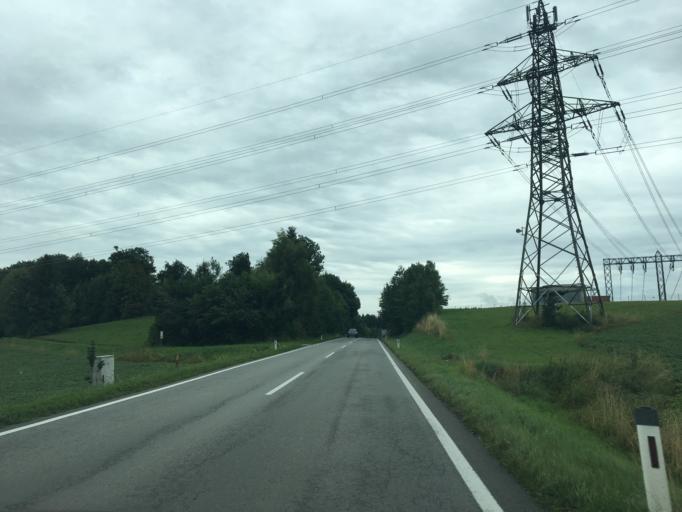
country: AT
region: Salzburg
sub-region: Politischer Bezirk Salzburg-Umgebung
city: Dorfbeuern
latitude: 48.0952
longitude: 12.9914
